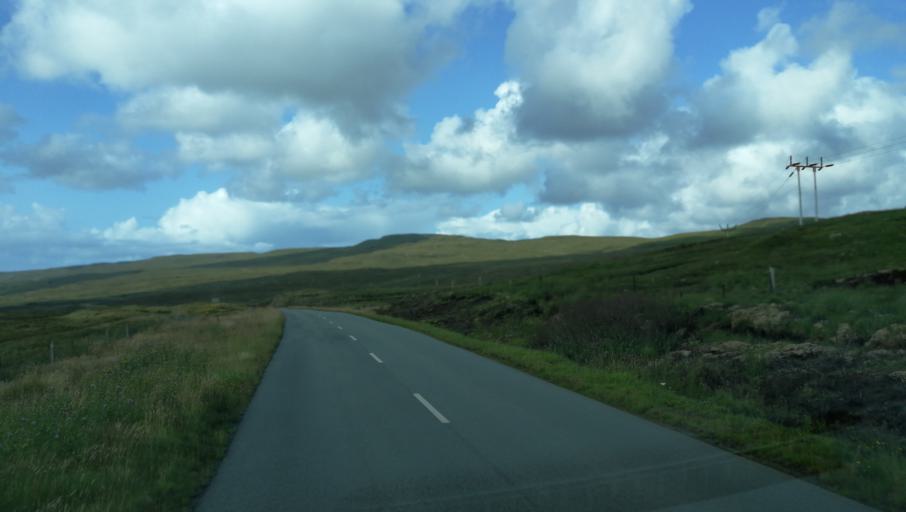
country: GB
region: Scotland
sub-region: Highland
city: Isle of Skye
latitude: 57.4642
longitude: -6.5423
